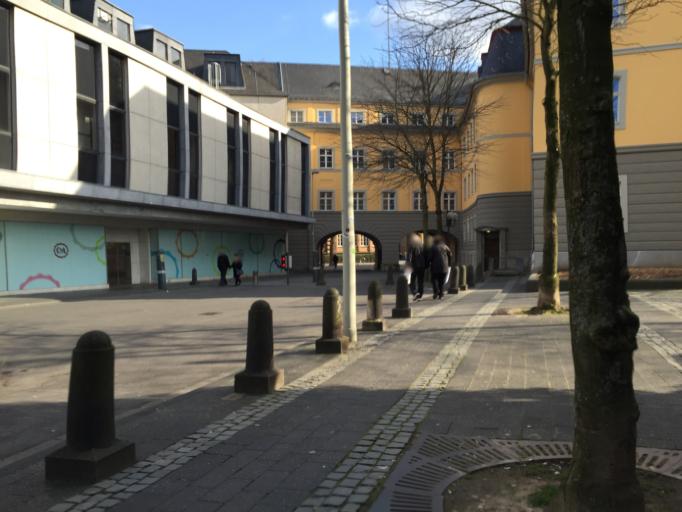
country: DE
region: North Rhine-Westphalia
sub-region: Regierungsbezirk Koln
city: Bonn
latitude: 50.7354
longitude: 7.0971
